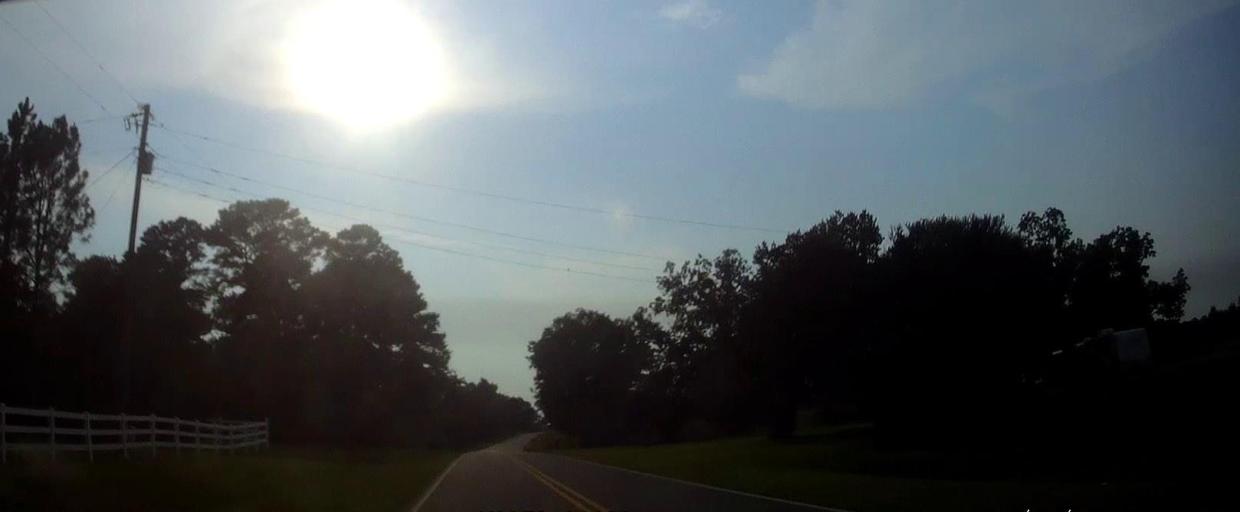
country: US
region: Georgia
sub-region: Laurens County
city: Dublin
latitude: 32.4805
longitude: -82.9615
